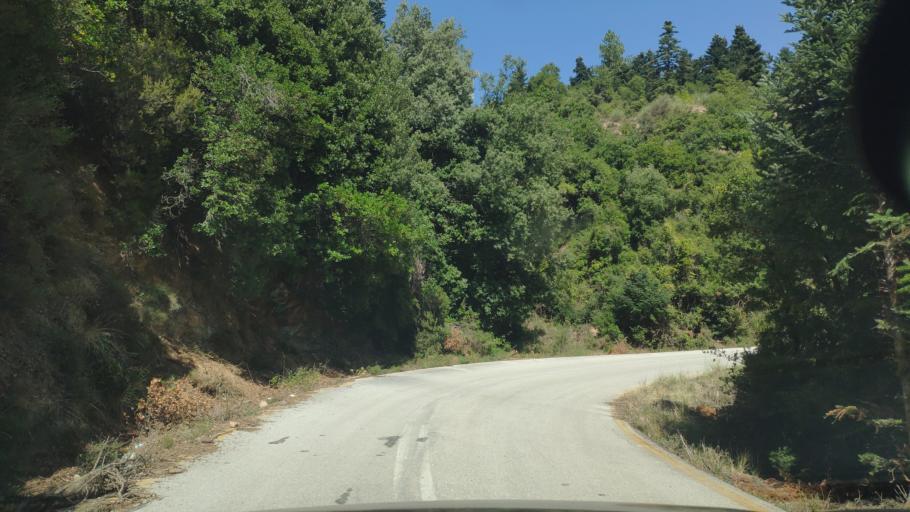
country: GR
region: Peloponnese
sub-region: Nomos Korinthias
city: Nemea
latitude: 37.8609
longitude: 22.3837
